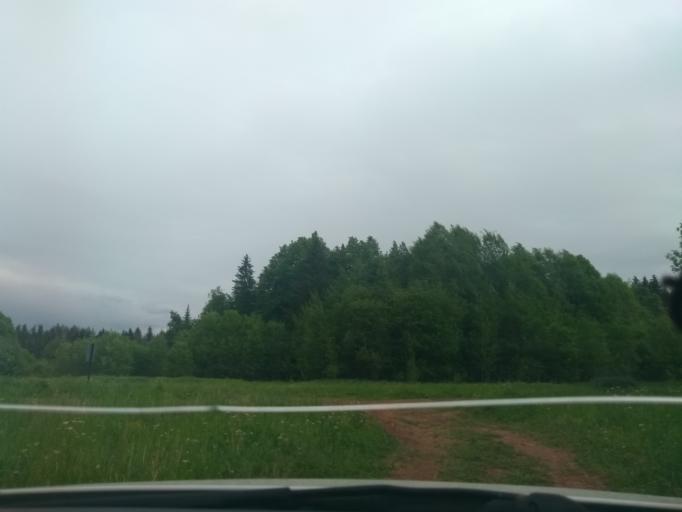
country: RU
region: Perm
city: Ferma
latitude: 57.9794
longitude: 56.3392
